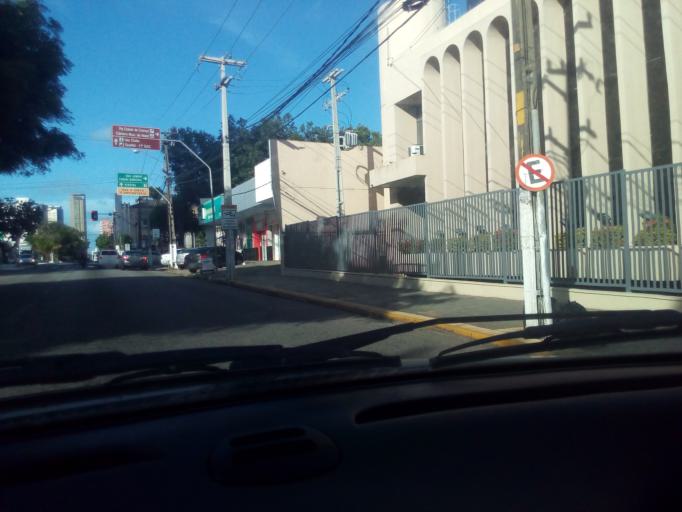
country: BR
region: Rio Grande do Norte
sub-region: Natal
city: Natal
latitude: -5.7889
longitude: -35.2048
